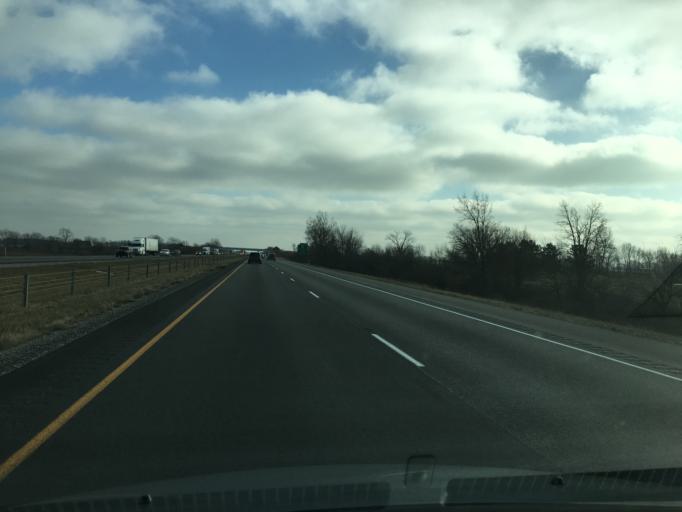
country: US
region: Indiana
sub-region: Clinton County
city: Mulberry
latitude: 40.2777
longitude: -86.6826
